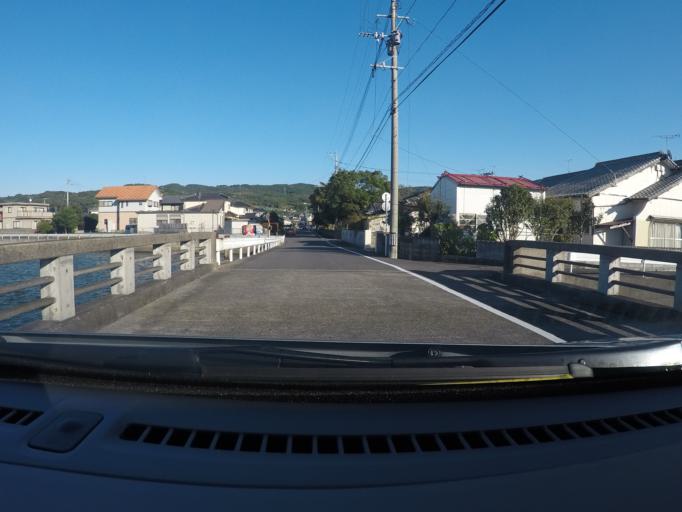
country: JP
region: Kumamoto
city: Minamata
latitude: 32.1765
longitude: 130.3775
